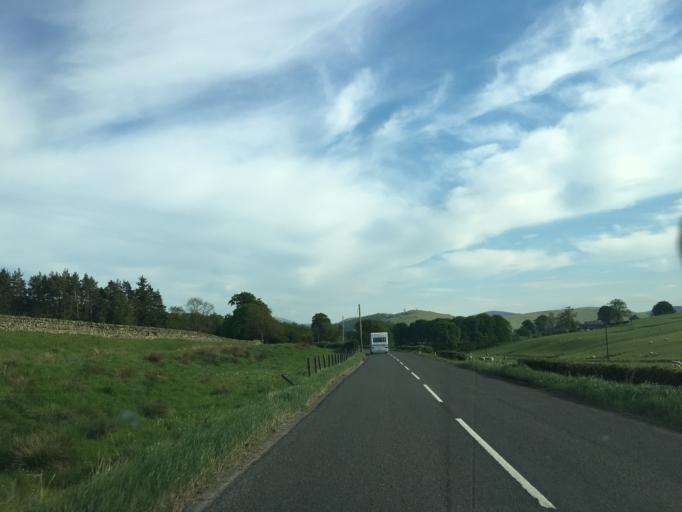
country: GB
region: Scotland
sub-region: South Lanarkshire
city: Biggar
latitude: 55.6233
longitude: -3.4148
